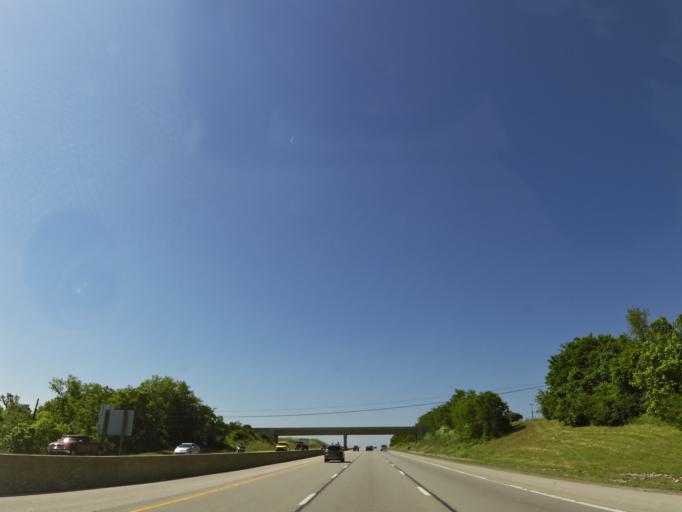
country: US
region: Kentucky
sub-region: Madison County
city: Berea
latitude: 37.6439
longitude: -84.3148
